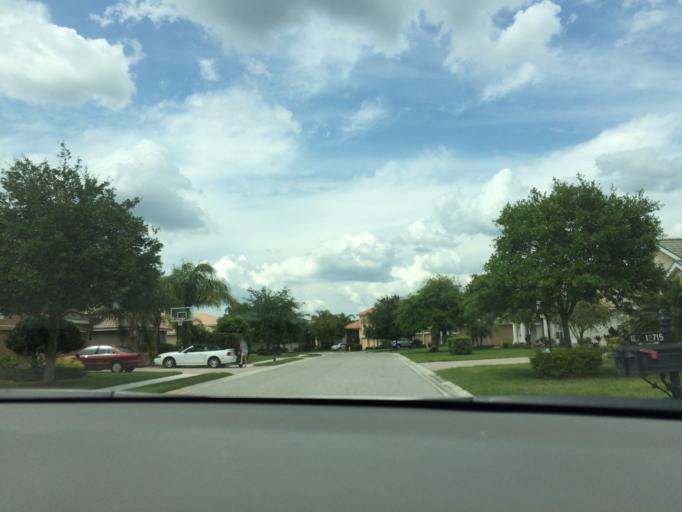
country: US
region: Florida
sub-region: Manatee County
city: Ellenton
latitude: 27.5067
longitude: -82.4136
